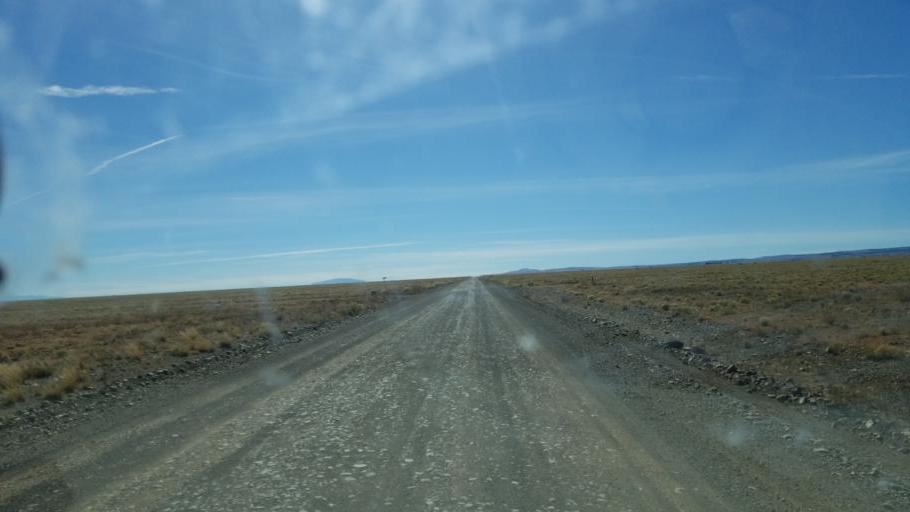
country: US
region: Colorado
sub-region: Rio Grande County
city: Monte Vista
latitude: 37.3697
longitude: -106.1493
